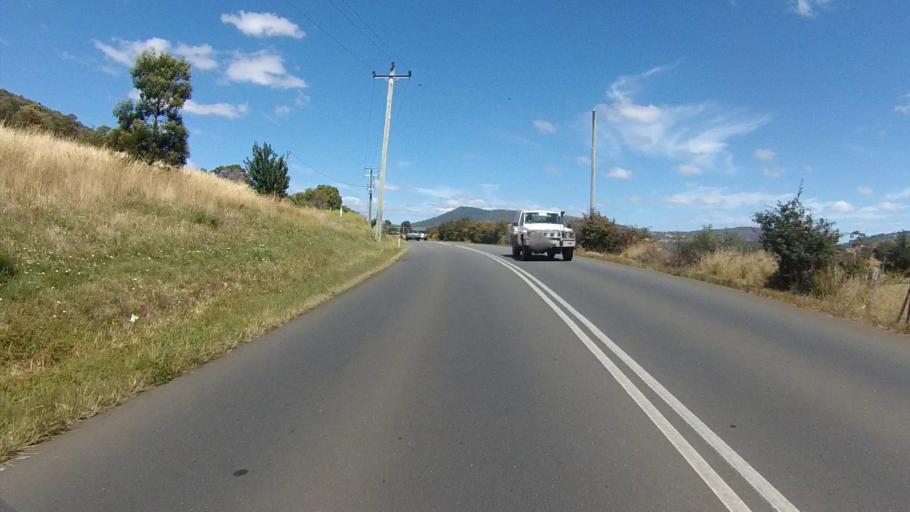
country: AU
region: Tasmania
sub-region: Clarence
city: Cambridge
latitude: -42.7406
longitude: 147.4234
